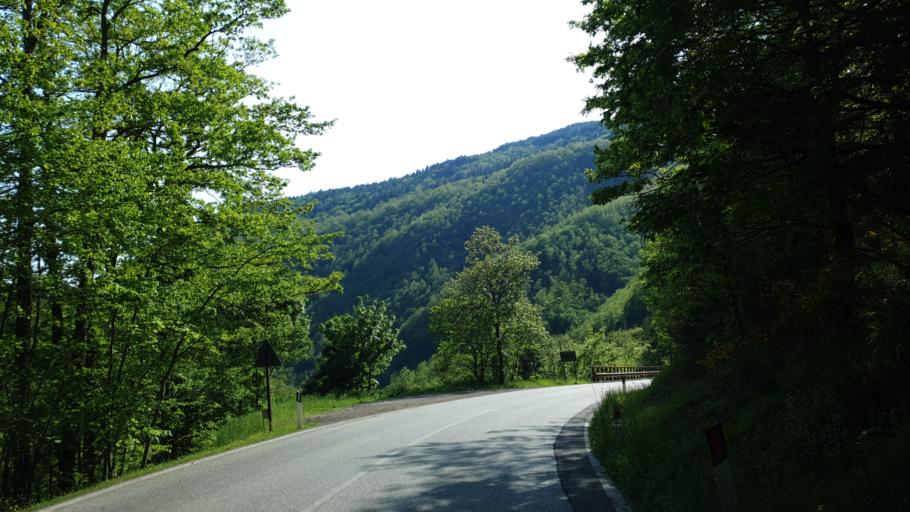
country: IT
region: Tuscany
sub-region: Province of Arezzo
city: Soci
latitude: 43.7881
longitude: 11.8737
